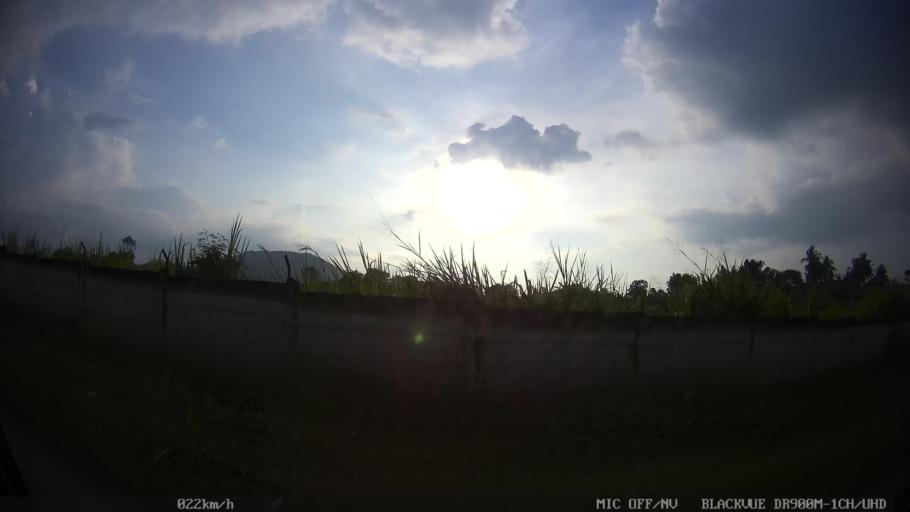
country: ID
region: Lampung
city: Panjang
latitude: -5.3967
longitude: 105.3535
